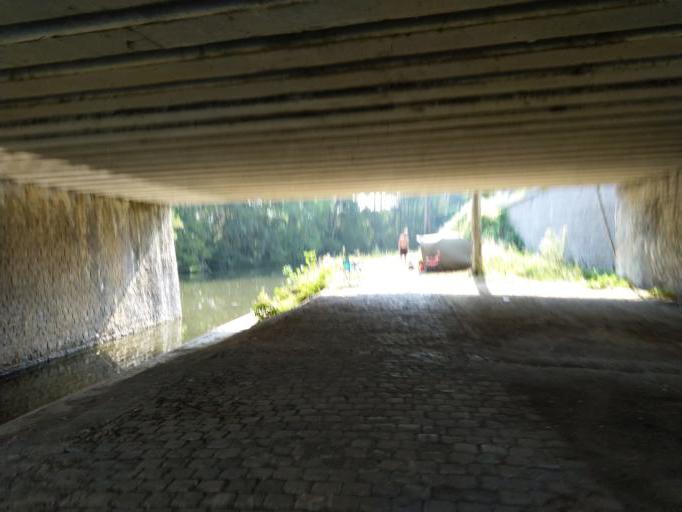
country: BE
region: Wallonia
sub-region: Province du Hainaut
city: Seneffe
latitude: 50.5647
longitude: 4.2810
